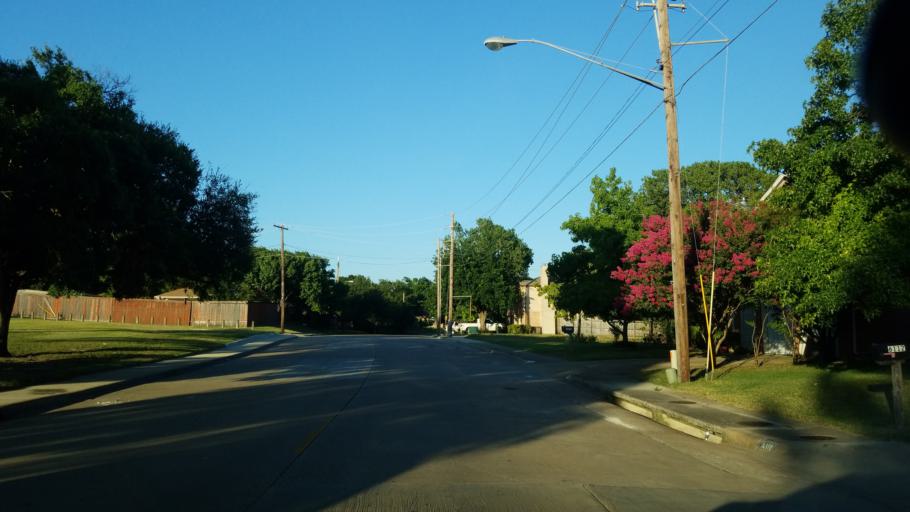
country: US
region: Texas
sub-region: Dallas County
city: Balch Springs
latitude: 32.7855
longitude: -96.6986
